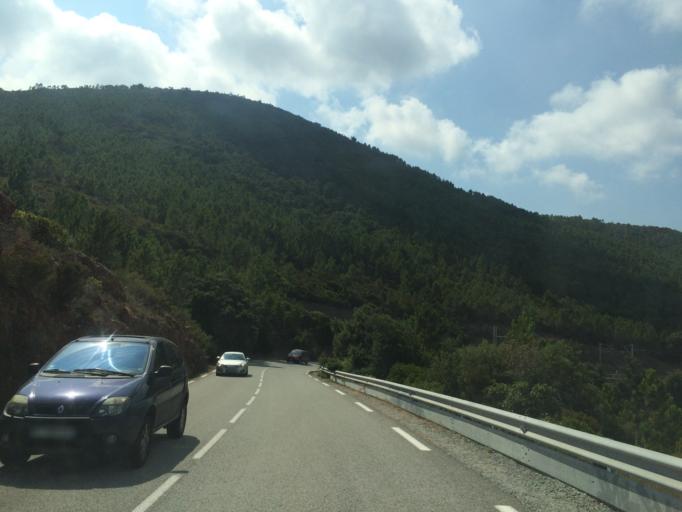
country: FR
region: Provence-Alpes-Cote d'Azur
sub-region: Departement des Alpes-Maritimes
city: Theoule-sur-Mer
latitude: 43.4565
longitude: 6.9211
